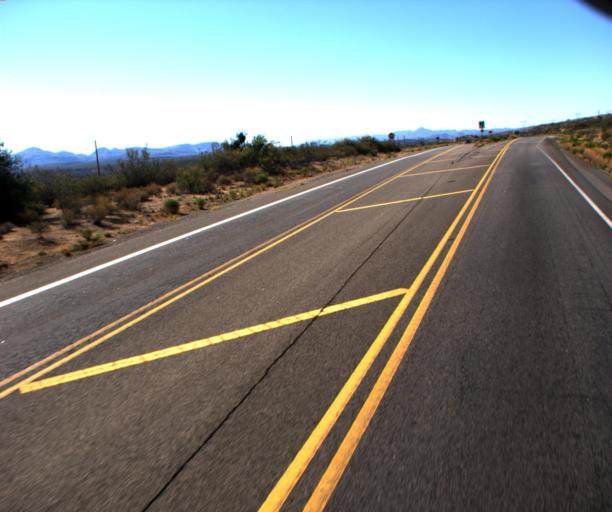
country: US
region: Arizona
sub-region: Yavapai County
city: Bagdad
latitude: 34.7671
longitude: -113.6195
